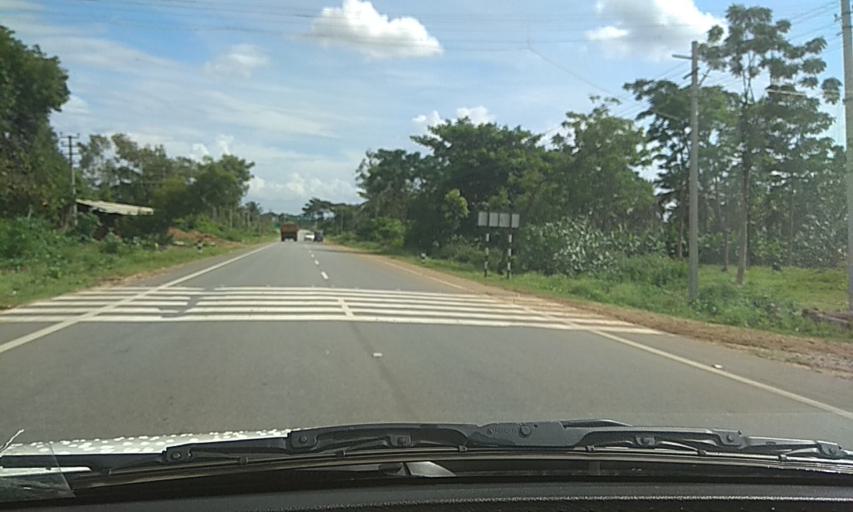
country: IN
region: Karnataka
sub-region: Mandya
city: Maddur
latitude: 12.6603
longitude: 77.0531
